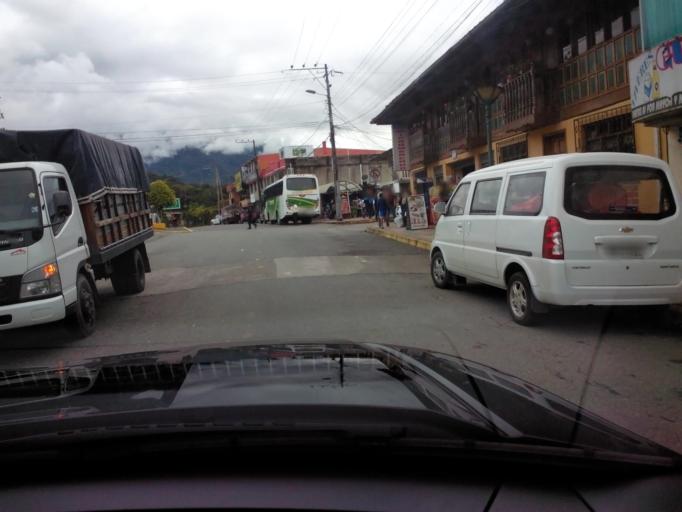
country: EC
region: Napo
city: Archidona
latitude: -0.4644
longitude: -77.8913
